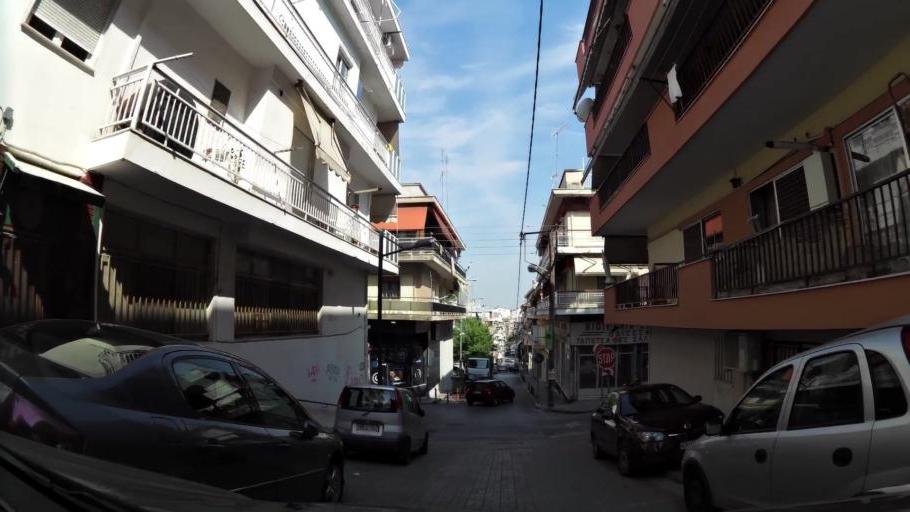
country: GR
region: Central Macedonia
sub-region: Nomos Thessalonikis
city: Sykies
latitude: 40.6500
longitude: 22.9527
